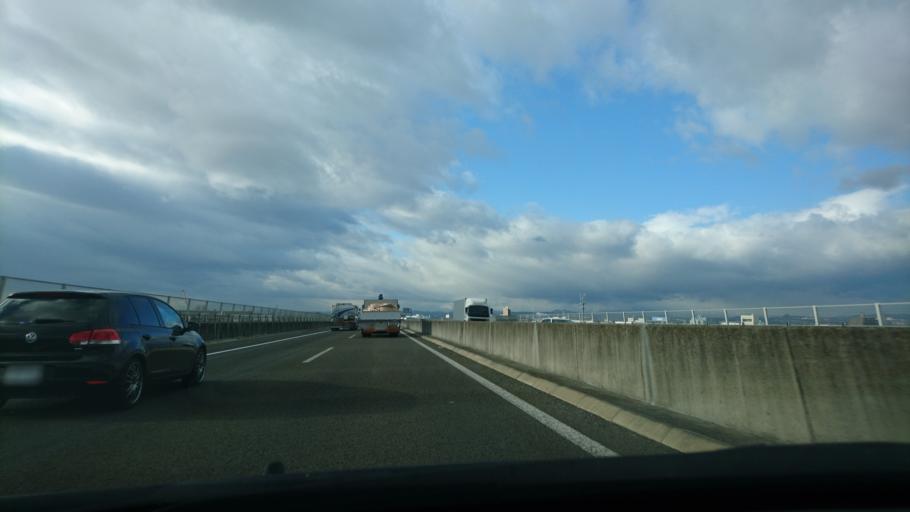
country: JP
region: Miyagi
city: Rifu
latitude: 38.2637
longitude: 140.9712
